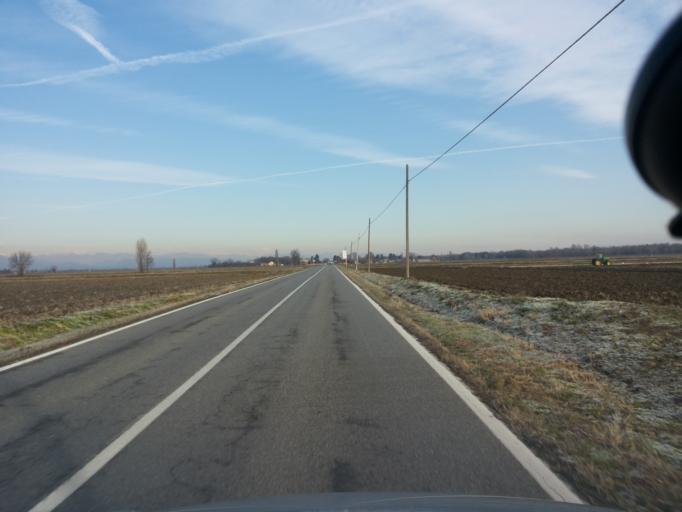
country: IT
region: Piedmont
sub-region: Provincia di Vercelli
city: Oldenico
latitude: 45.4115
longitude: 8.3778
